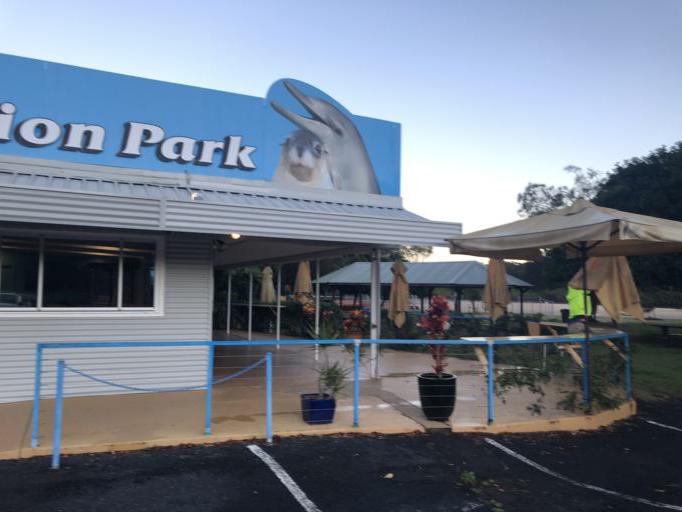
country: AU
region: New South Wales
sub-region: Coffs Harbour
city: Coffs Harbour
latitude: -30.2983
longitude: 153.1368
